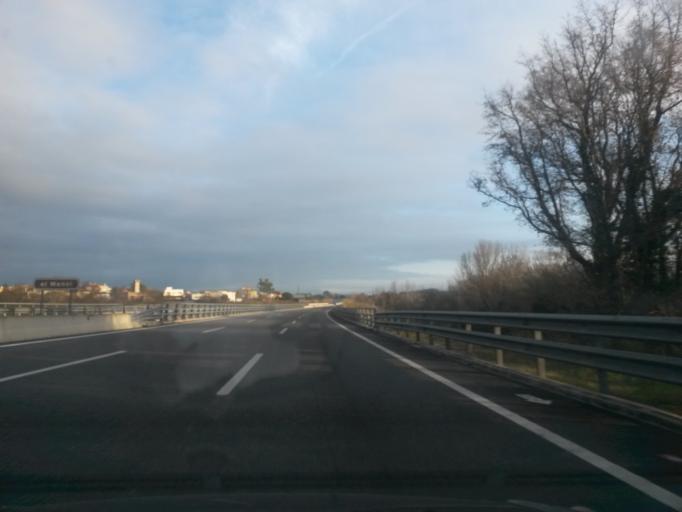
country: ES
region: Catalonia
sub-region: Provincia de Girona
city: Vilafant
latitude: 42.2422
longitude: 2.9384
